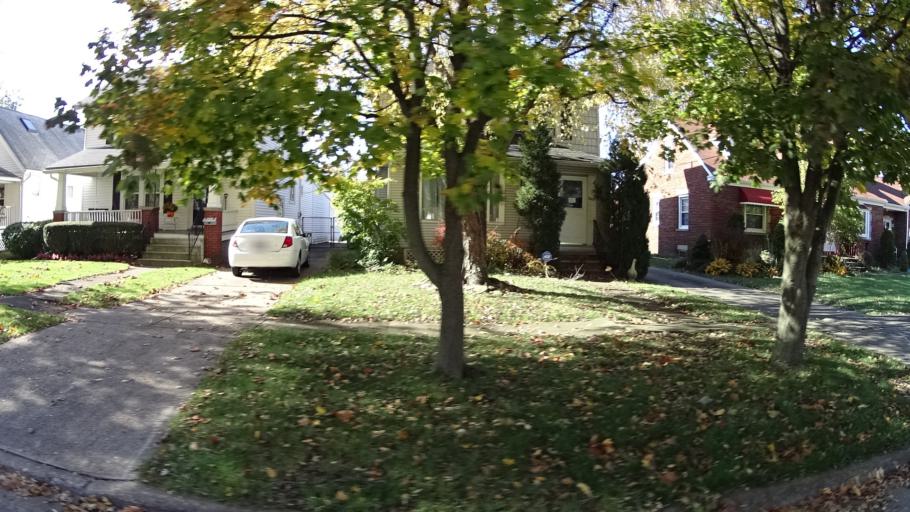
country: US
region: Ohio
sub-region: Lorain County
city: Lorain
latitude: 41.4593
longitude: -82.1985
